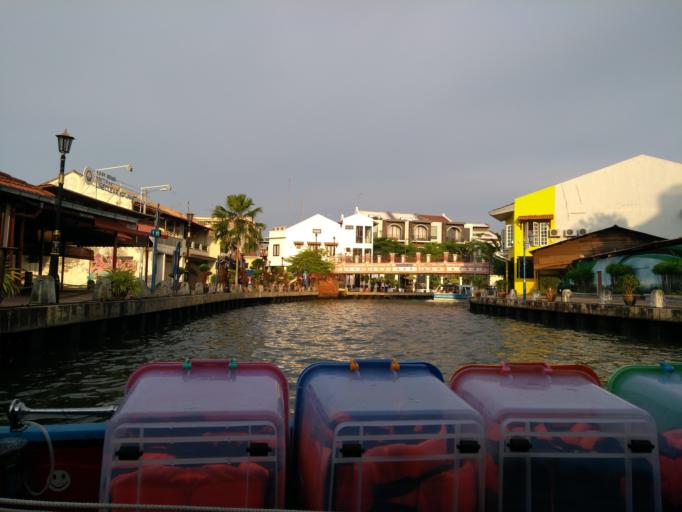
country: MY
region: Melaka
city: Malacca
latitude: 2.1974
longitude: 102.2499
